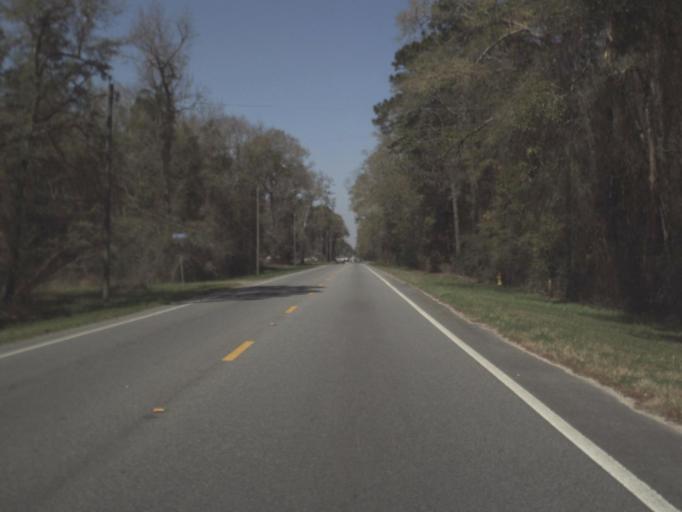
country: US
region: Florida
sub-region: Leon County
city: Woodville
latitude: 30.2753
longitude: -84.2392
